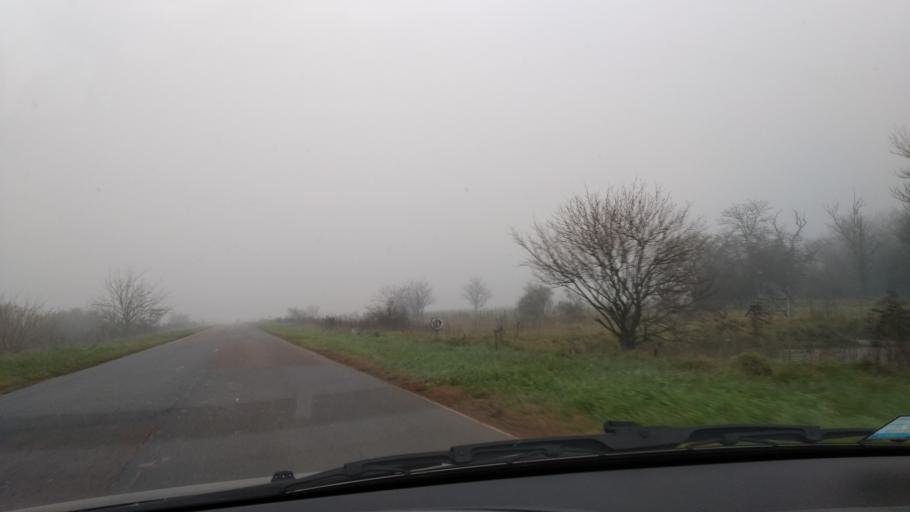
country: AR
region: Buenos Aires
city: San Miguel del Monte
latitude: -35.3098
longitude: -58.5985
